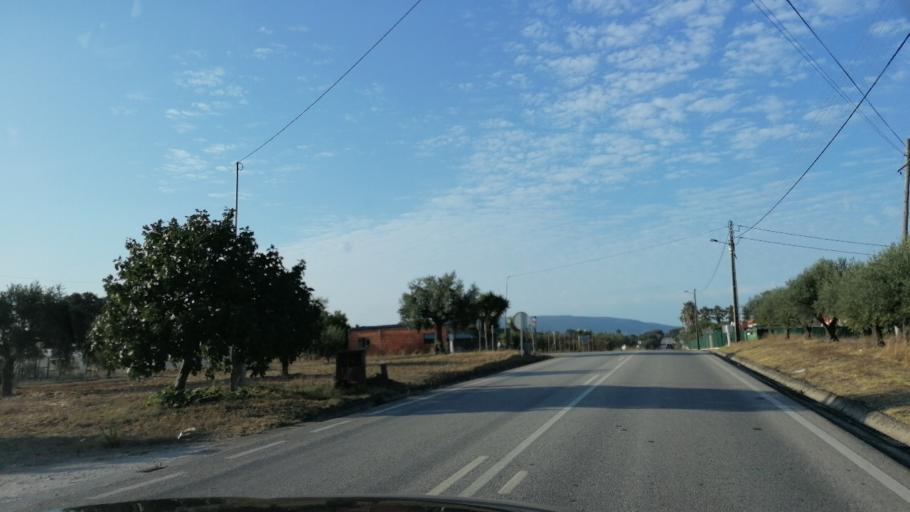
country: PT
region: Santarem
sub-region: Alcanena
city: Alcanena
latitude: 39.4180
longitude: -8.6364
